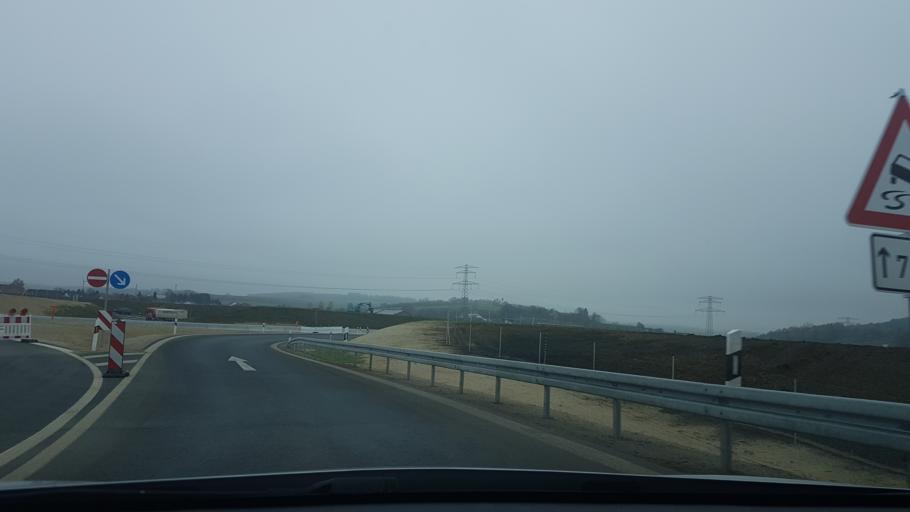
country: DE
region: Bavaria
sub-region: Lower Bavaria
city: Essenbach
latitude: 48.6174
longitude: 12.2311
